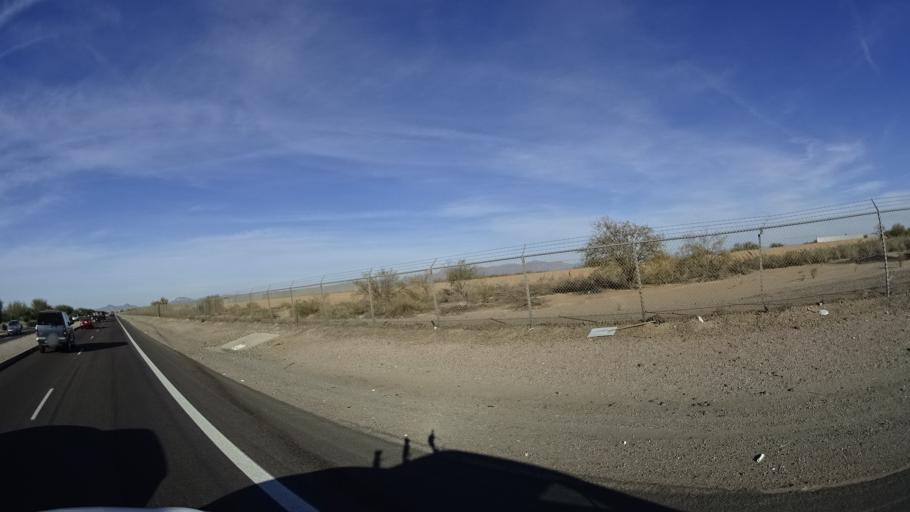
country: US
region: Arizona
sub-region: Maricopa County
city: Queen Creek
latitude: 33.2936
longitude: -111.6350
